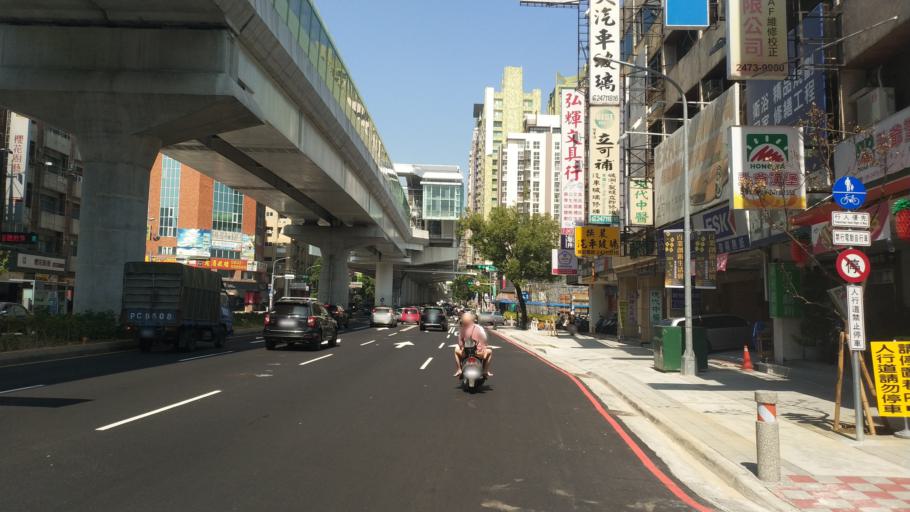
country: TW
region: Taiwan
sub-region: Taichung City
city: Taichung
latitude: 24.1392
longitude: 120.6469
